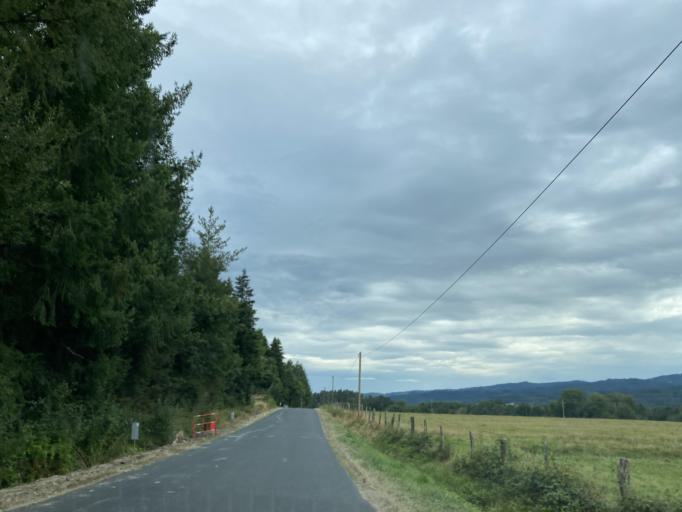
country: FR
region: Auvergne
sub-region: Departement du Puy-de-Dome
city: Marsac-en-Livradois
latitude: 45.5084
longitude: 3.7429
